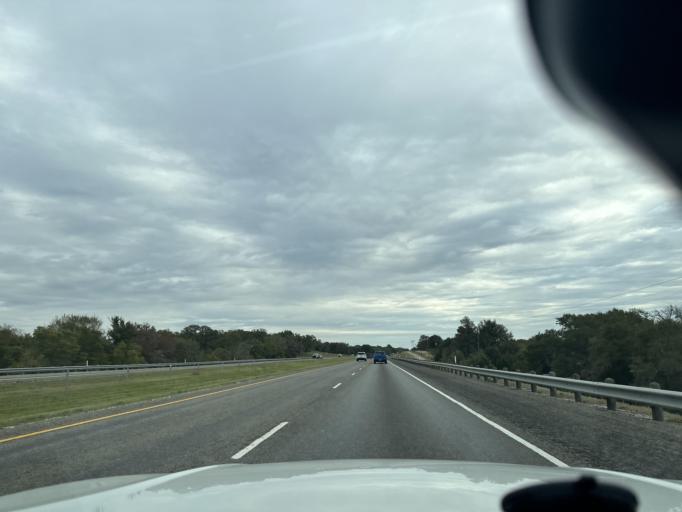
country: US
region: Texas
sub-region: Washington County
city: Brenham
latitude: 30.1853
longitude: -96.4920
